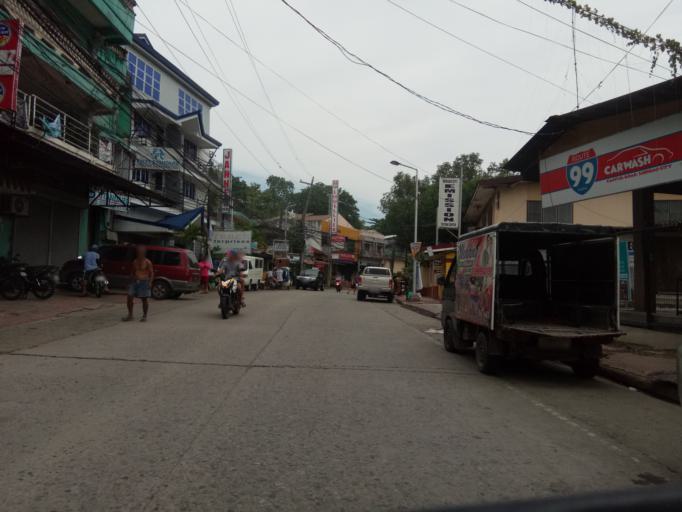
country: PH
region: Caraga
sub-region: Province of Surigao del Norte
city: Surigao
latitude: 9.7858
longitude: 125.4918
